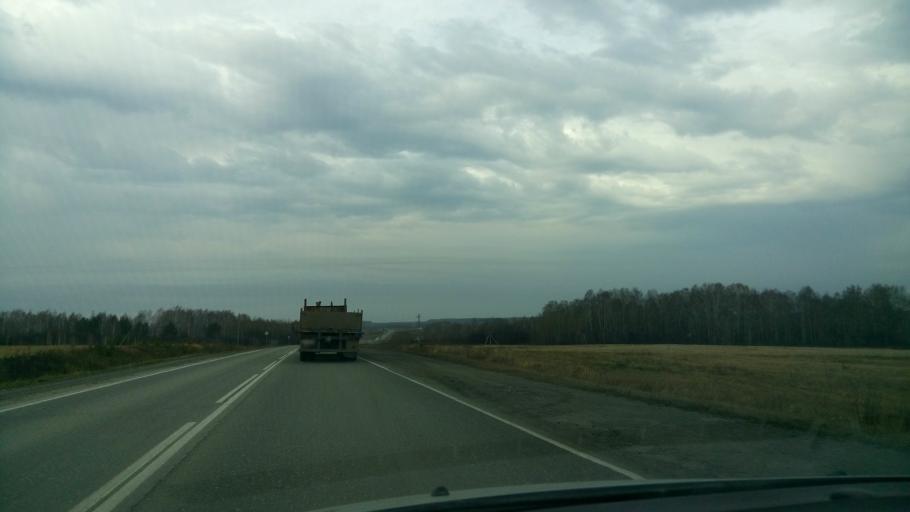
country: RU
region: Sverdlovsk
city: Kamyshlov
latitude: 56.8675
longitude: 62.7543
